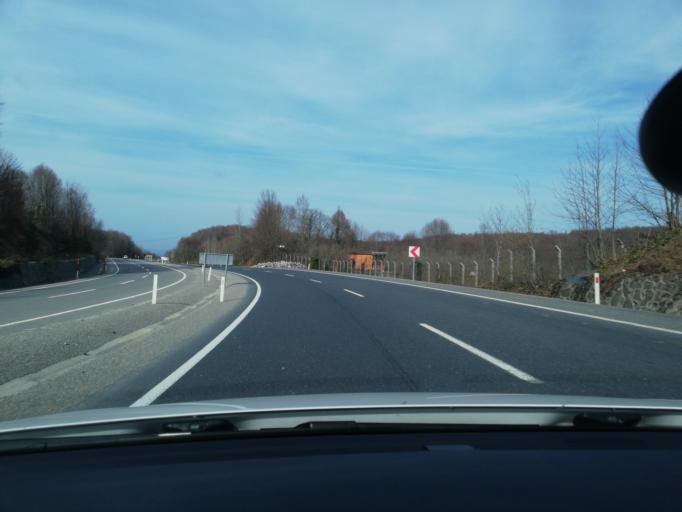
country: TR
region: Zonguldak
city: Kozlu
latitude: 41.3339
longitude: 31.6277
